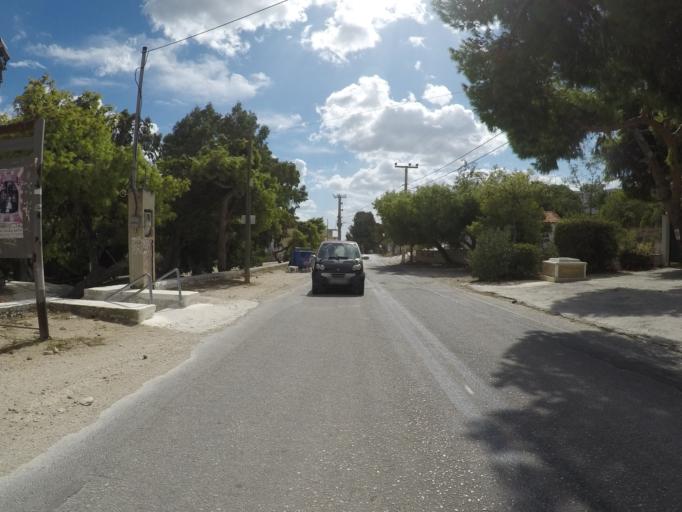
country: GR
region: Attica
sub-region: Nomarchia Anatolikis Attikis
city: Agios Dimitrios Kropias
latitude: 37.8065
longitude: 23.8681
